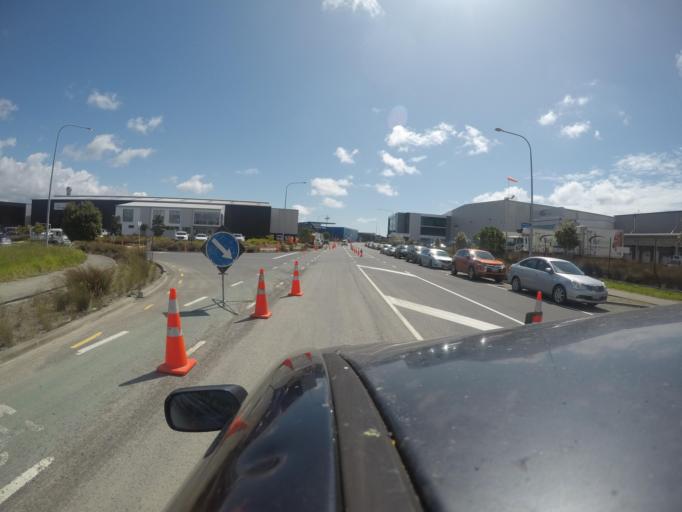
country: NZ
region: Auckland
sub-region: Auckland
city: Rosebank
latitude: -36.8062
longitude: 174.6322
